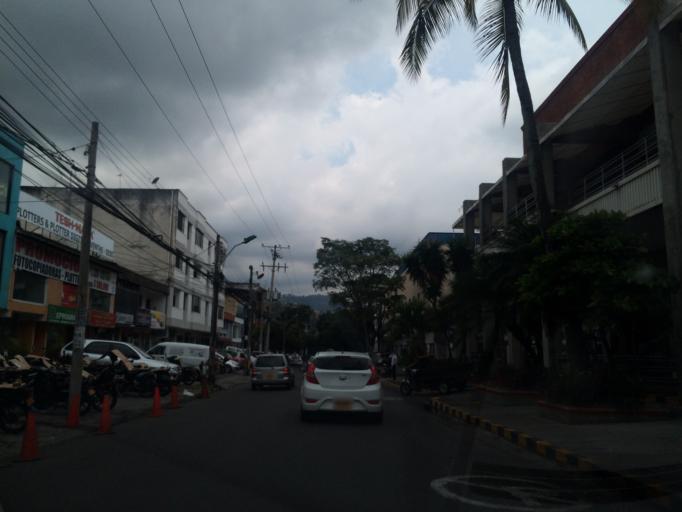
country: CO
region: Valle del Cauca
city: Cali
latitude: 3.4663
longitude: -76.5276
